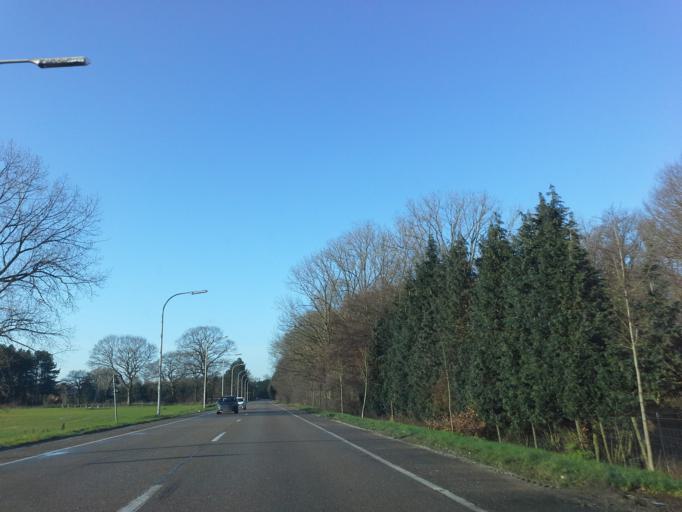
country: BE
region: Flanders
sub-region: Provincie Antwerpen
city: Olen
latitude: 51.1576
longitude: 4.8576
